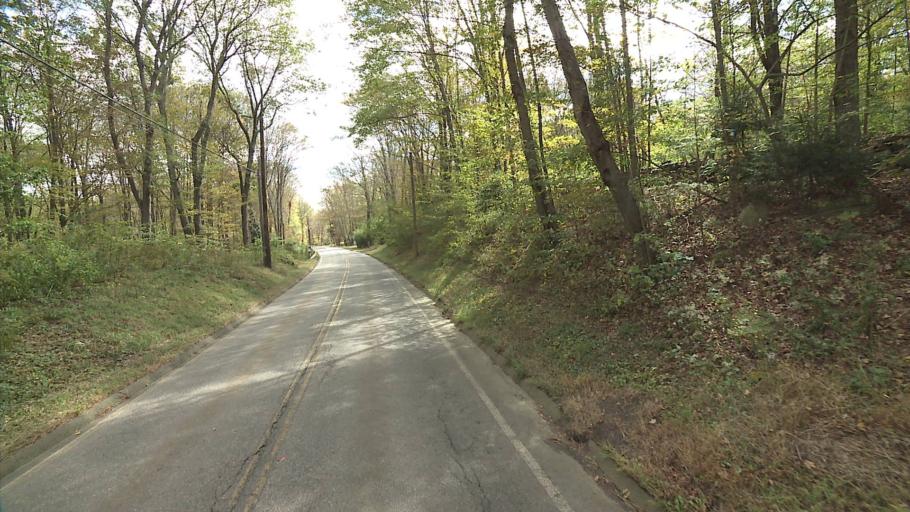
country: US
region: Connecticut
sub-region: Middlesex County
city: Durham
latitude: 41.4253
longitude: -72.6341
